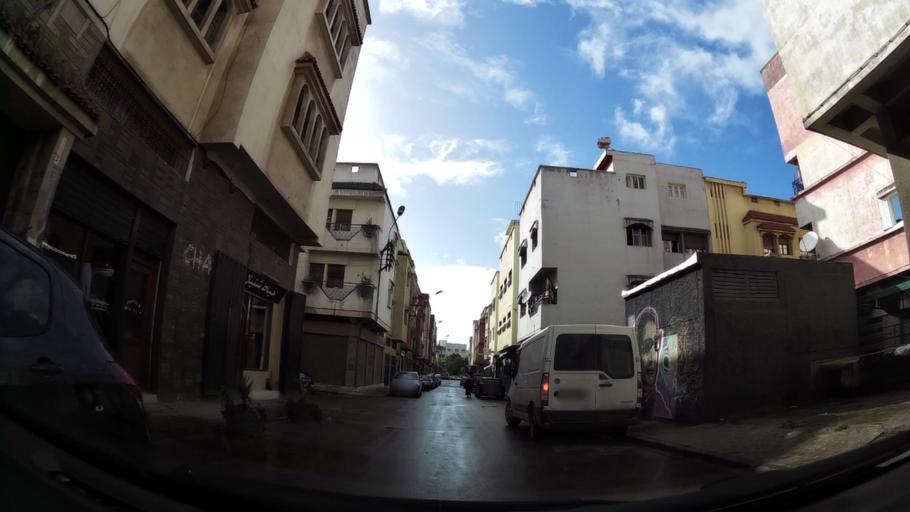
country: MA
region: Grand Casablanca
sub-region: Casablanca
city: Casablanca
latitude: 33.5466
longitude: -7.5979
